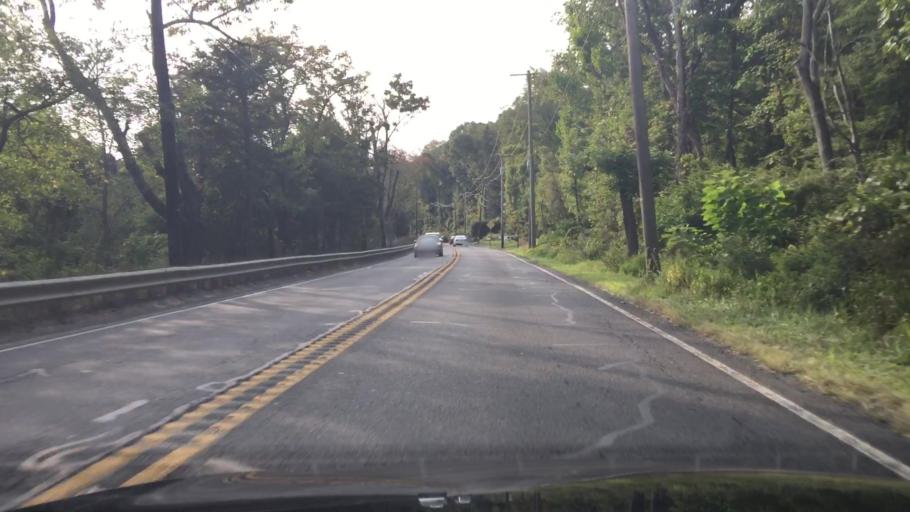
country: US
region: New Jersey
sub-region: Hunterdon County
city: Lambertville
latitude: 40.3165
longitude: -74.8959
